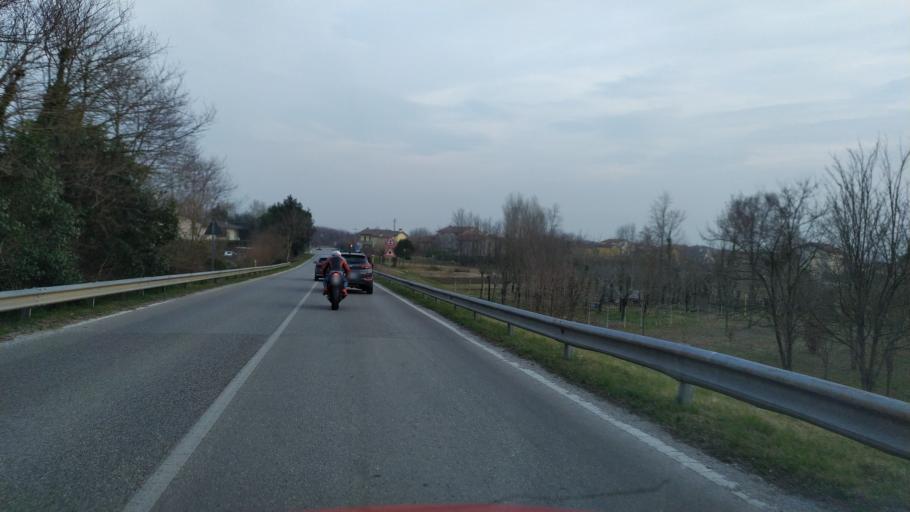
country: IT
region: Veneto
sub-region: Provincia di Vicenza
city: Dueville
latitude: 45.6485
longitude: 11.5536
